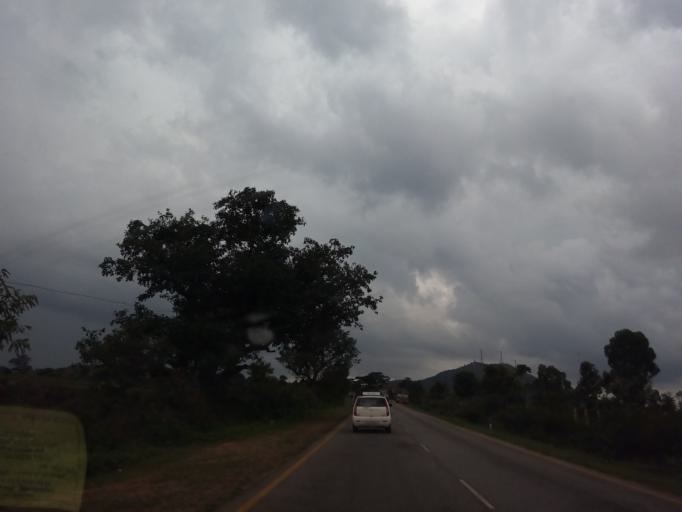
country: IN
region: Karnataka
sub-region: Hassan
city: Hassan
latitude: 13.0808
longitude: 76.0453
